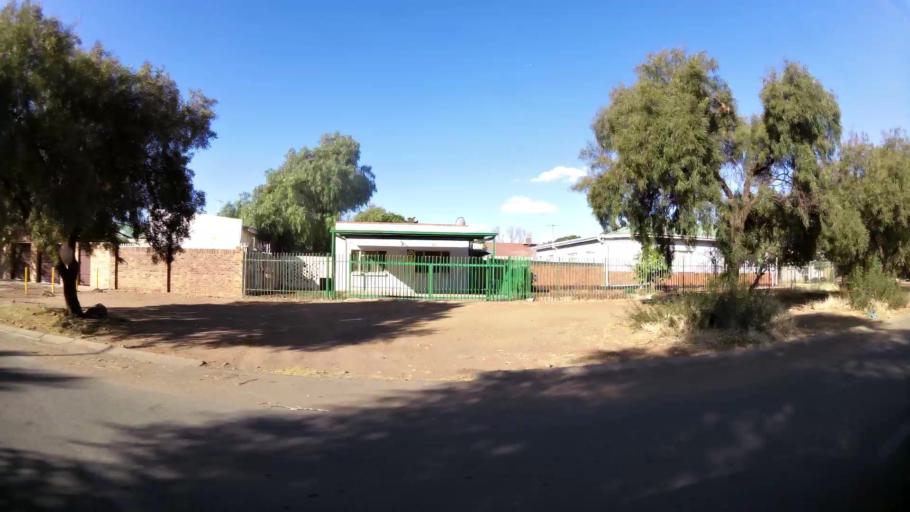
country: ZA
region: Northern Cape
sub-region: Frances Baard District Municipality
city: Kimberley
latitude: -28.7477
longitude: 24.7591
